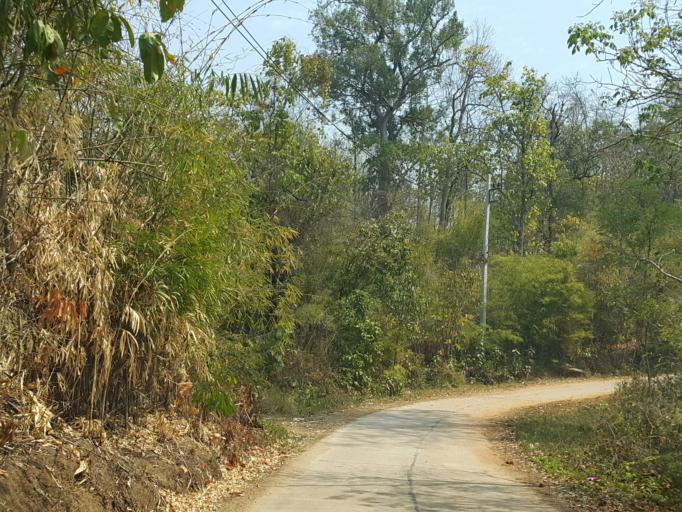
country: TH
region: Lampang
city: Mueang Pan
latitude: 18.8193
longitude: 99.4678
